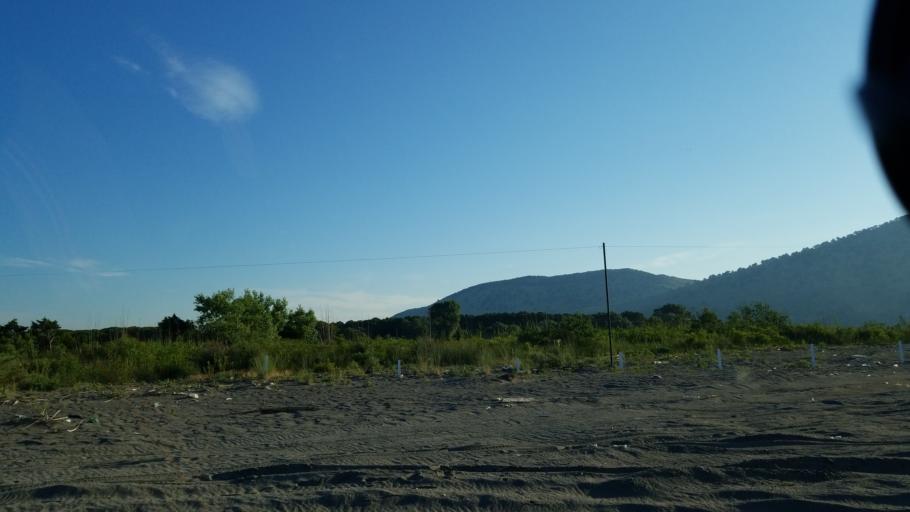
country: AL
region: Shkoder
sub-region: Rrethi i Shkodres
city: Velipoje
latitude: 41.8594
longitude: 19.4447
